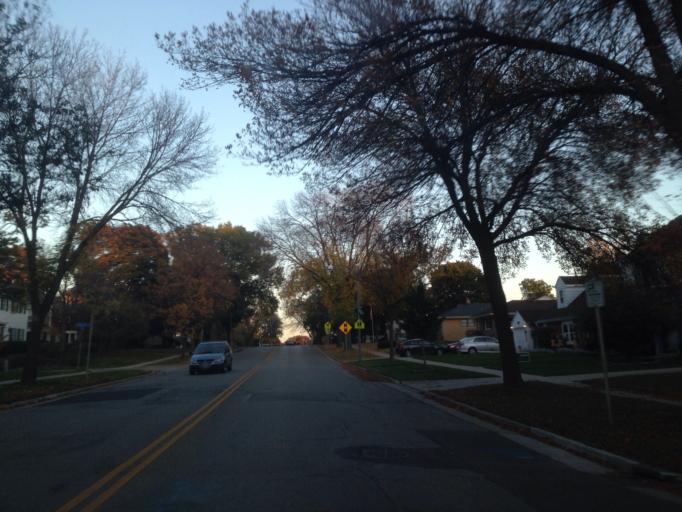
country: US
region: Wisconsin
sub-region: Milwaukee County
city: Wauwatosa
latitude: 43.0386
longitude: -88.0181
